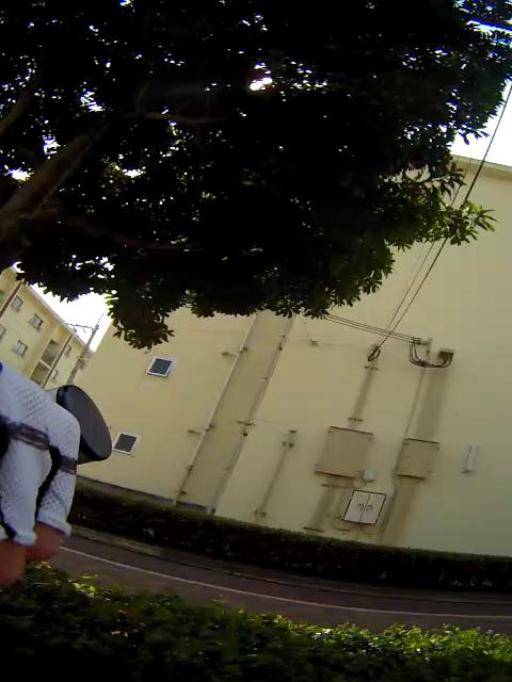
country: JP
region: Osaka
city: Yao
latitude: 34.6048
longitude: 135.5849
